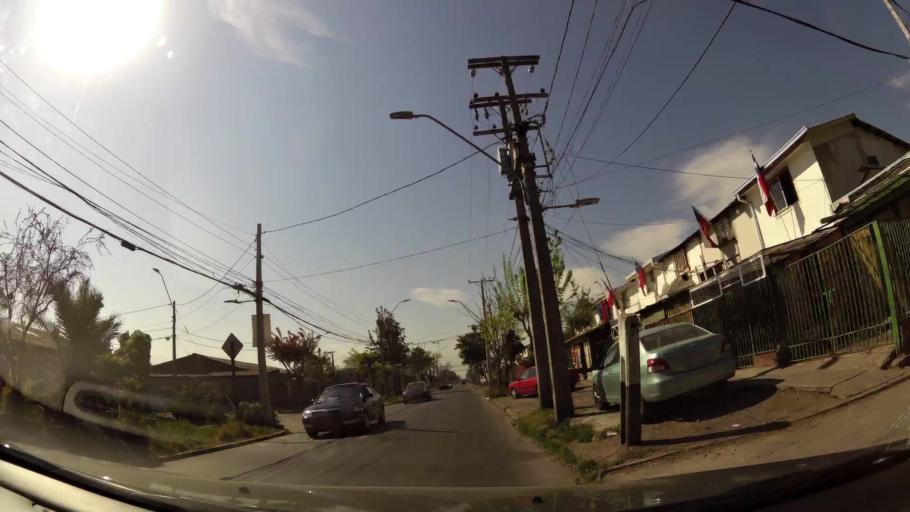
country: CL
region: Santiago Metropolitan
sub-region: Provincia de Maipo
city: San Bernardo
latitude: -33.5969
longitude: -70.6887
